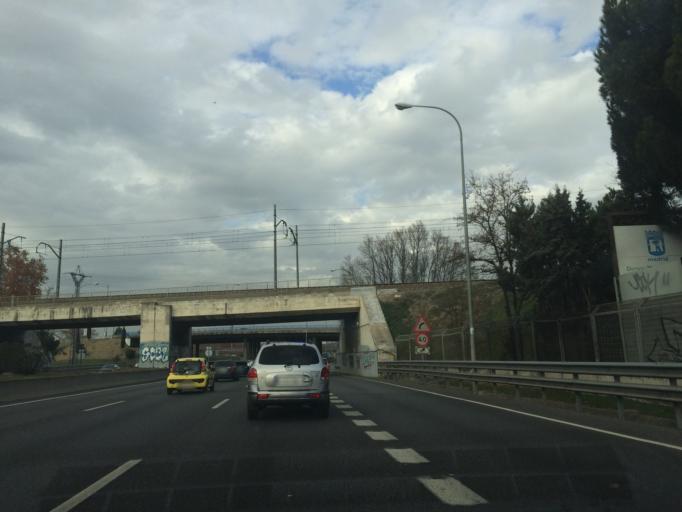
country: ES
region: Madrid
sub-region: Provincia de Madrid
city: Moncloa-Aravaca
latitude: 40.4332
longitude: -3.7377
